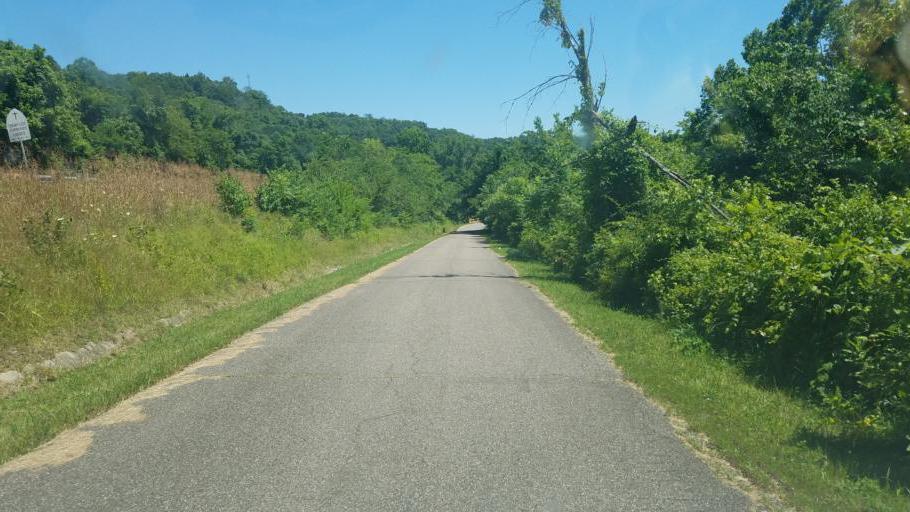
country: US
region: West Virginia
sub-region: Cabell County
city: Lesage
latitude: 38.5836
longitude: -82.2930
